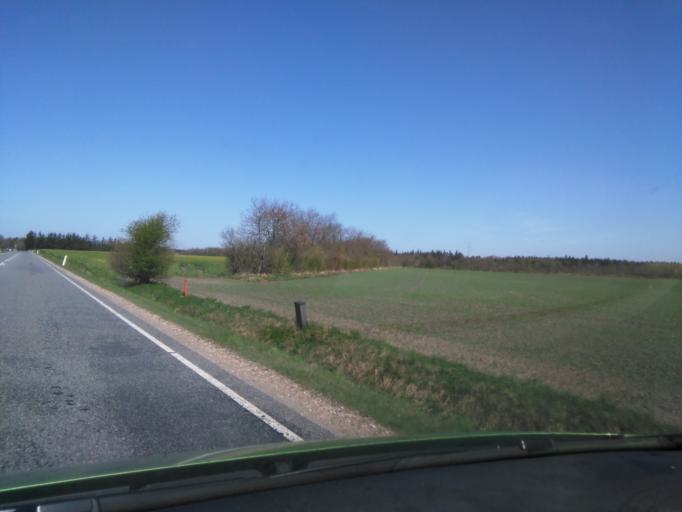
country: DK
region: South Denmark
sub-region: Varde Kommune
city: Olgod
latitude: 55.7151
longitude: 8.7393
